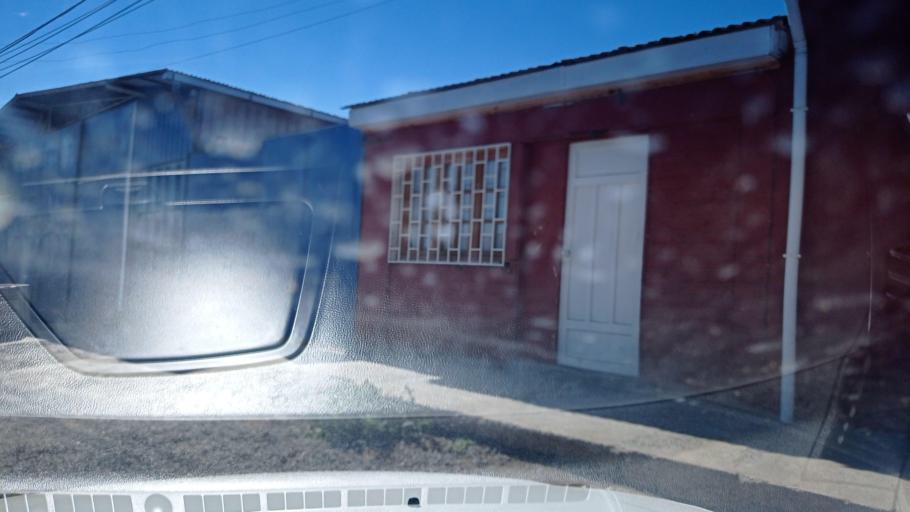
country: CL
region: O'Higgins
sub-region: Provincia de Colchagua
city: Santa Cruz
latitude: -34.3866
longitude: -71.9976
